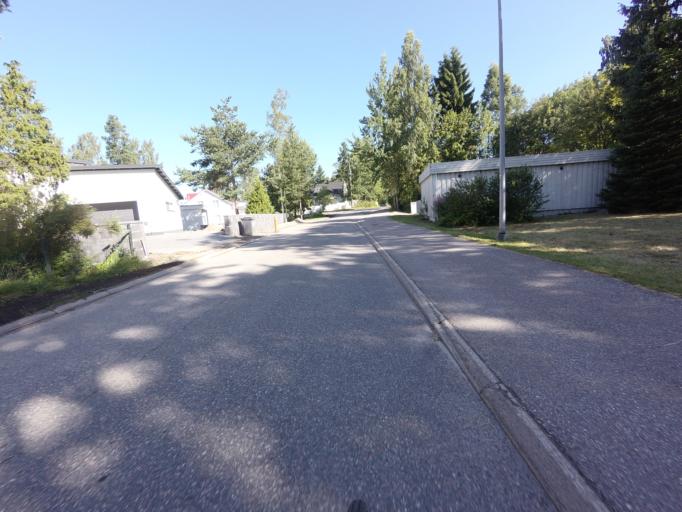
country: FI
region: Uusimaa
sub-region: Helsinki
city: Espoo
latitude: 60.1654
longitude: 24.6716
